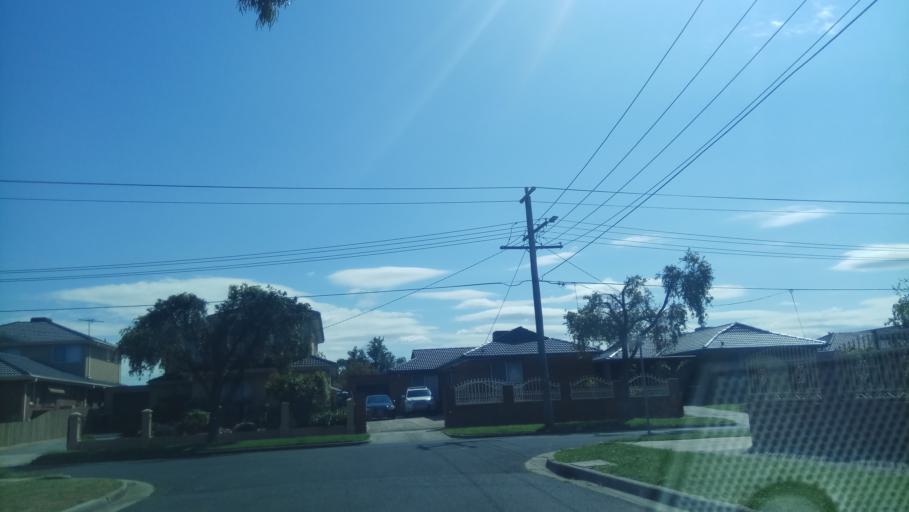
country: AU
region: Victoria
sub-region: Kingston
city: Clayton South
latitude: -37.9458
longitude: 145.1035
